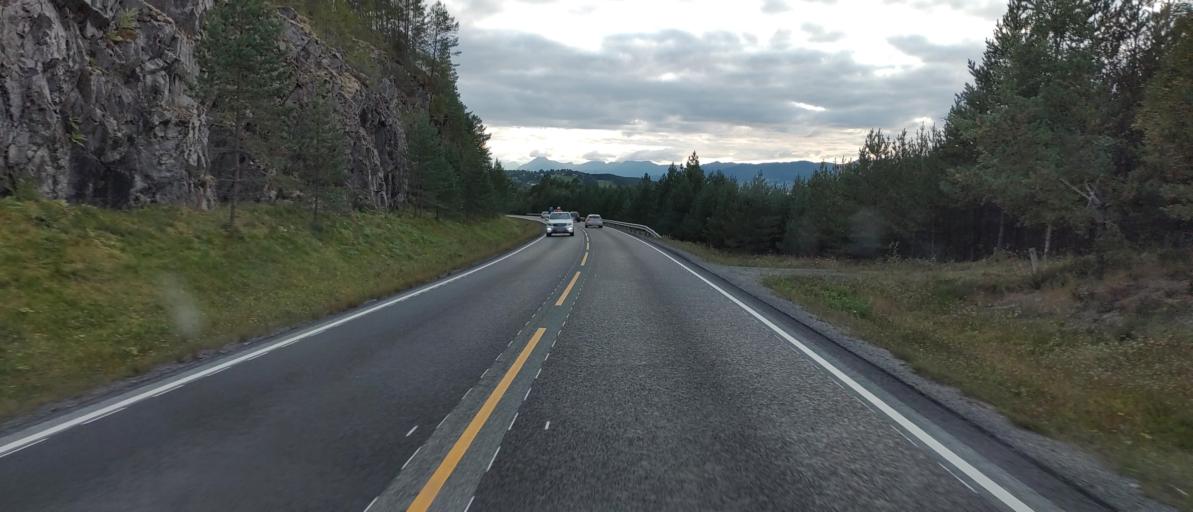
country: NO
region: More og Romsdal
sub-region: Molde
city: Hjelset
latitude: 62.7349
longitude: 7.3875
